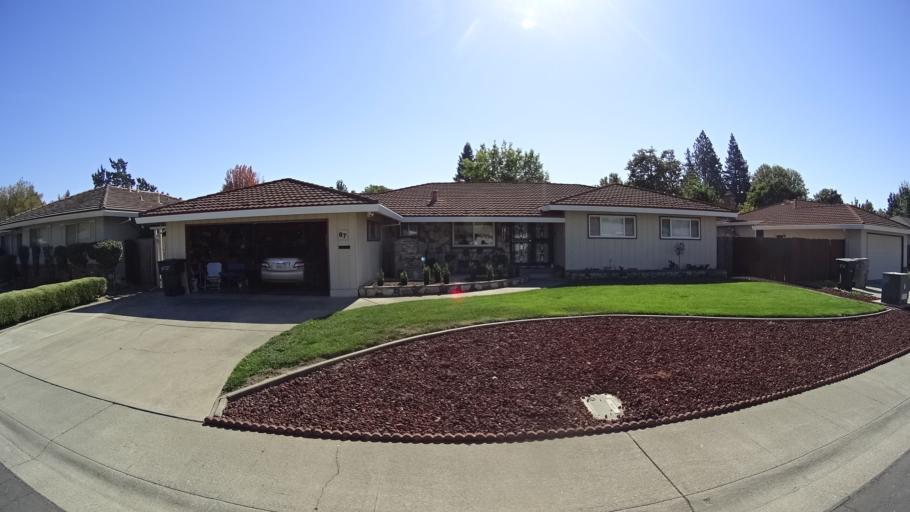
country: US
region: California
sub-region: Sacramento County
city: Parkway
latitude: 38.5084
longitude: -121.5253
